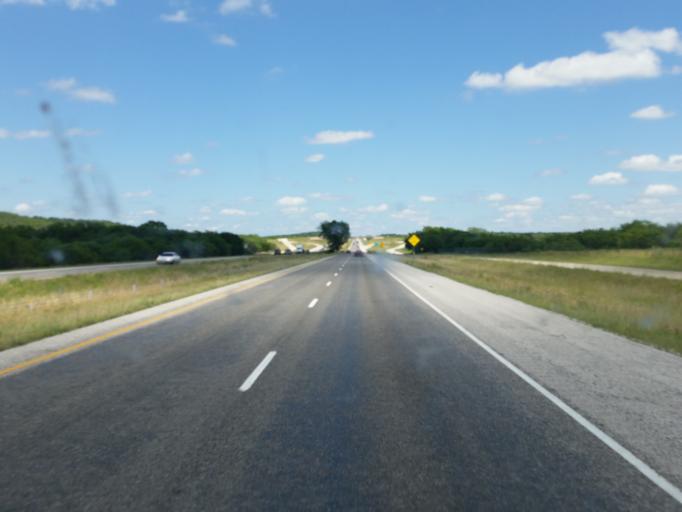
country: US
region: Texas
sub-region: Eastland County
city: Cisco
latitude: 32.3773
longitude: -99.1139
